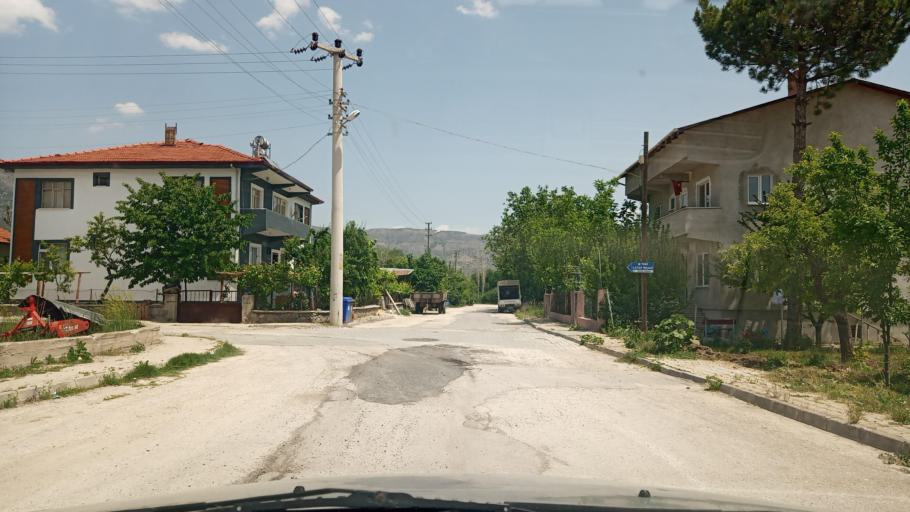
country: TR
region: Bolu
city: Seben
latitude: 40.4115
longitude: 31.5768
